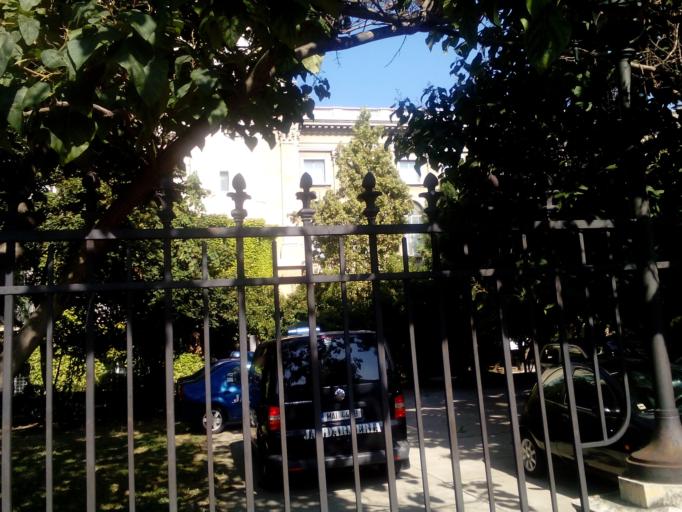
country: RO
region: Bucuresti
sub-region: Municipiul Bucuresti
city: Bucuresti
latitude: 44.4400
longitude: 26.0946
